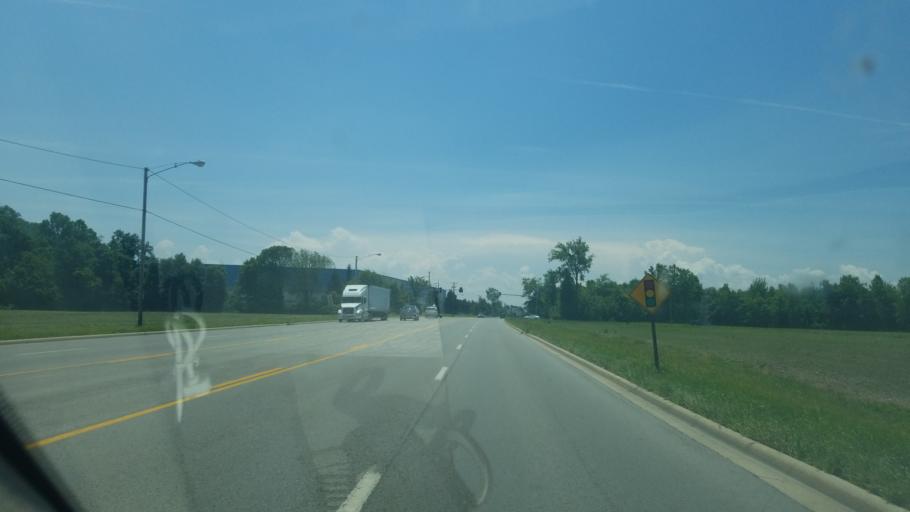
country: US
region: Ohio
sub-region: Hancock County
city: Findlay
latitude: 41.0747
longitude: -83.6175
